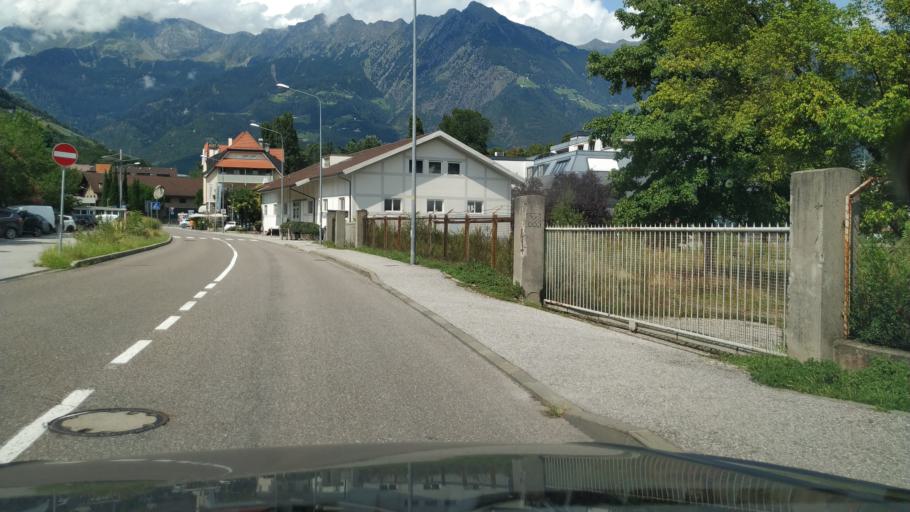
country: IT
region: Trentino-Alto Adige
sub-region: Bolzano
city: Marlengo
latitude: 46.6555
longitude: 11.1500
